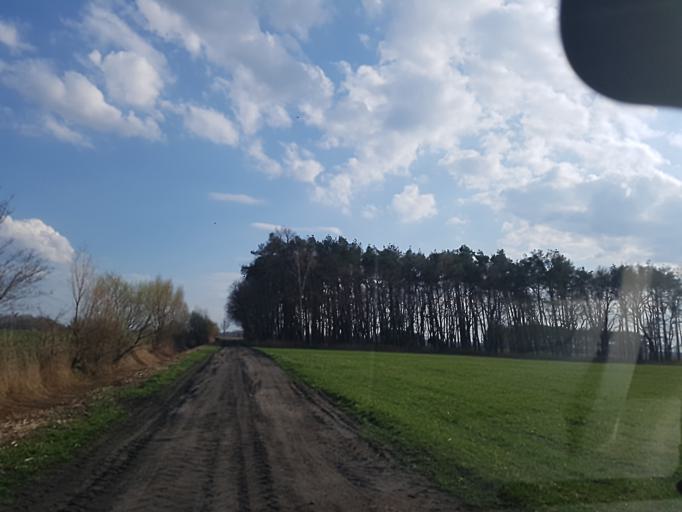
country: DE
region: Brandenburg
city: Schonborn
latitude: 51.6039
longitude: 13.5274
